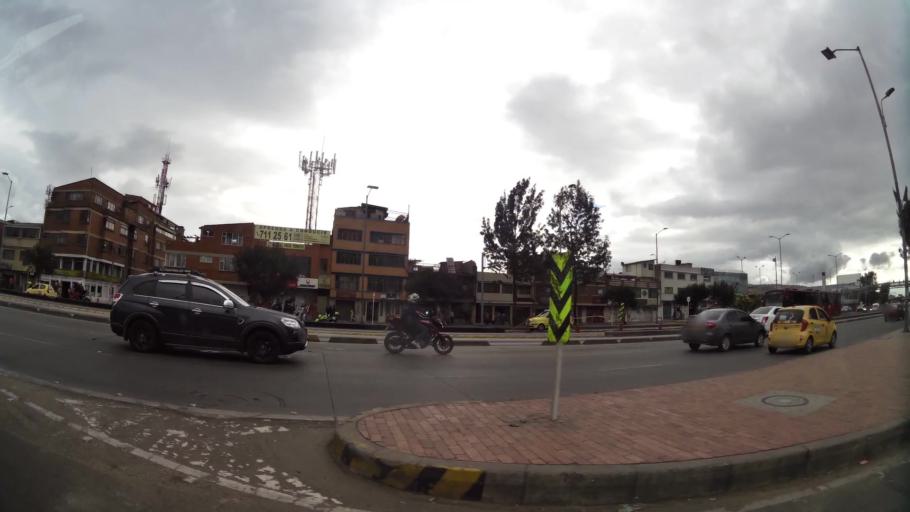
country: CO
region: Bogota D.C.
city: Bogota
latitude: 4.5957
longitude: -74.1403
